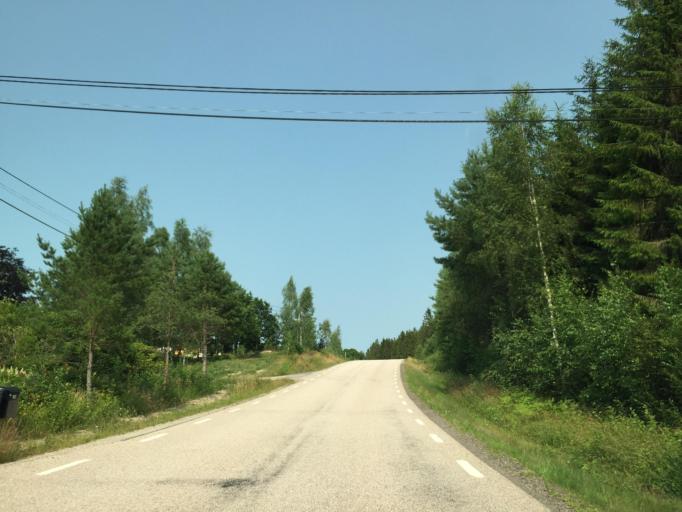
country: SE
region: Vaestra Goetaland
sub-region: Lilla Edets Kommun
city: Lilla Edet
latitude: 58.1596
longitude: 12.0696
